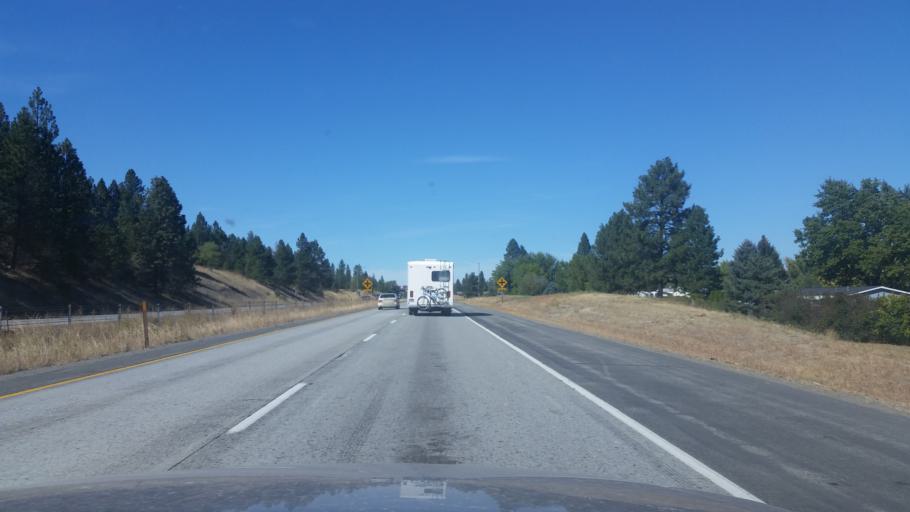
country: US
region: Washington
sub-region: Spokane County
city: Spokane
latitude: 47.6380
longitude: -117.4472
